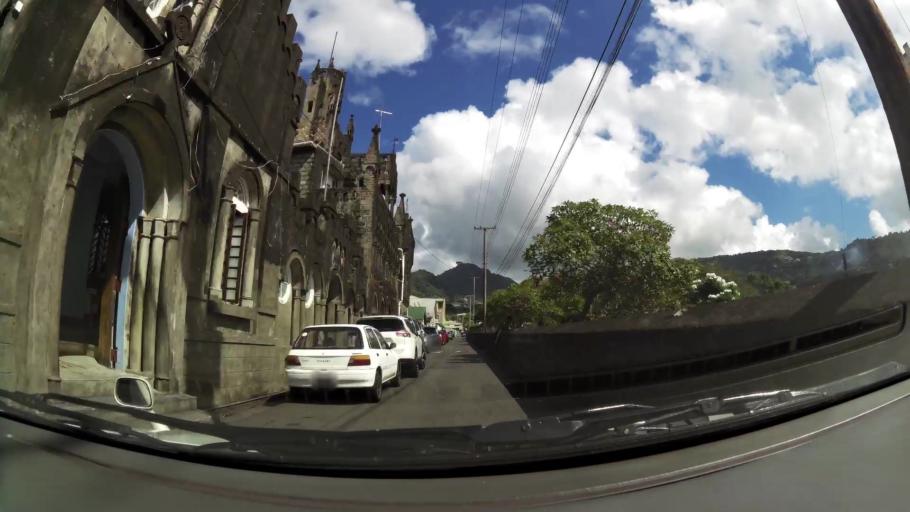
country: VC
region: Saint George
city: Kingstown
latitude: 13.1575
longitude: -61.2289
